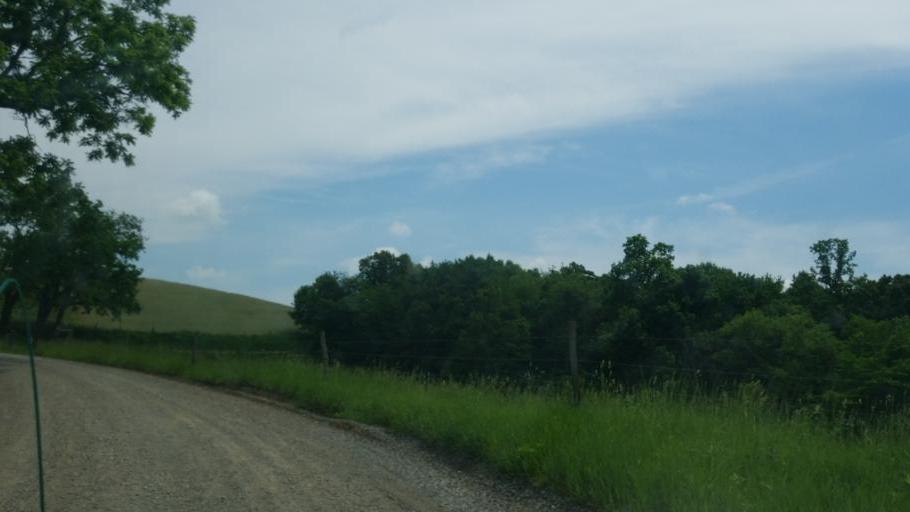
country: US
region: Ohio
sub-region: Holmes County
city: Millersburg
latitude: 40.4816
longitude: -81.7957
